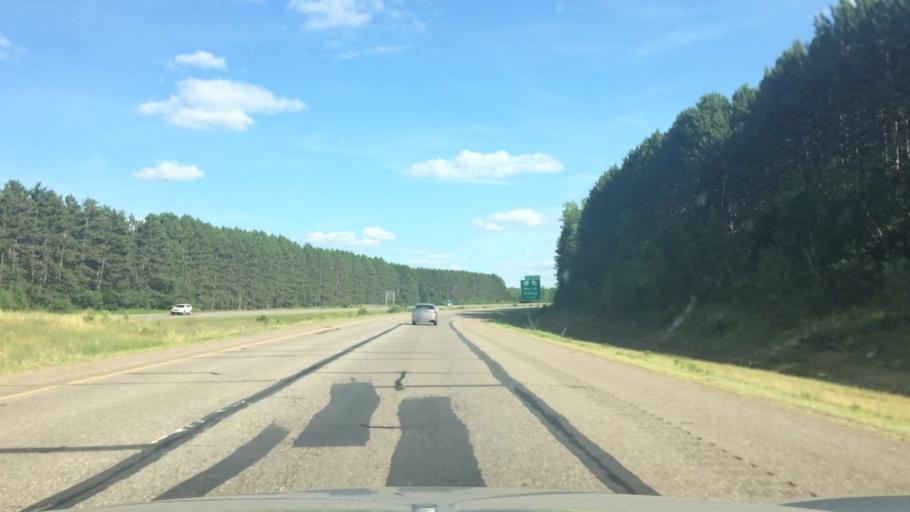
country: US
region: Wisconsin
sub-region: Lincoln County
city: Merrill
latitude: 45.1988
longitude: -89.6513
